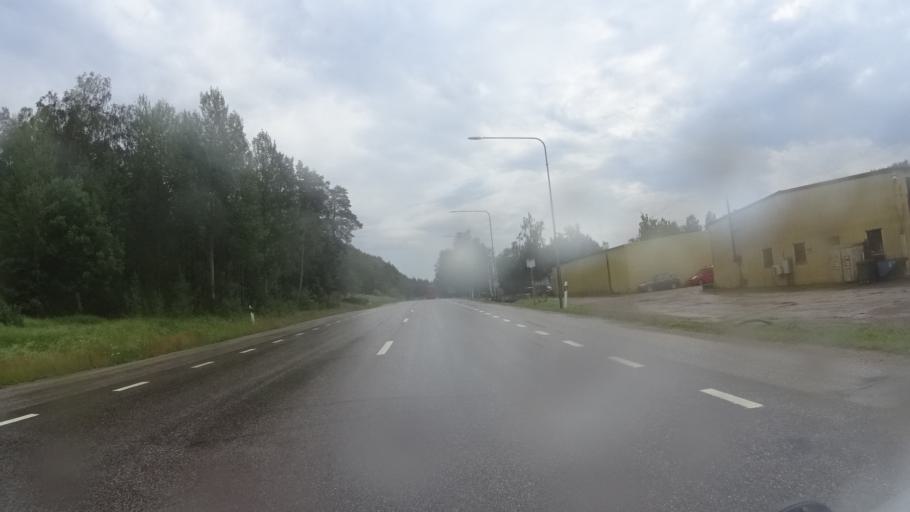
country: SE
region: OEstergoetland
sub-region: Kinda Kommun
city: Kisa
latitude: 57.9816
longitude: 15.6380
